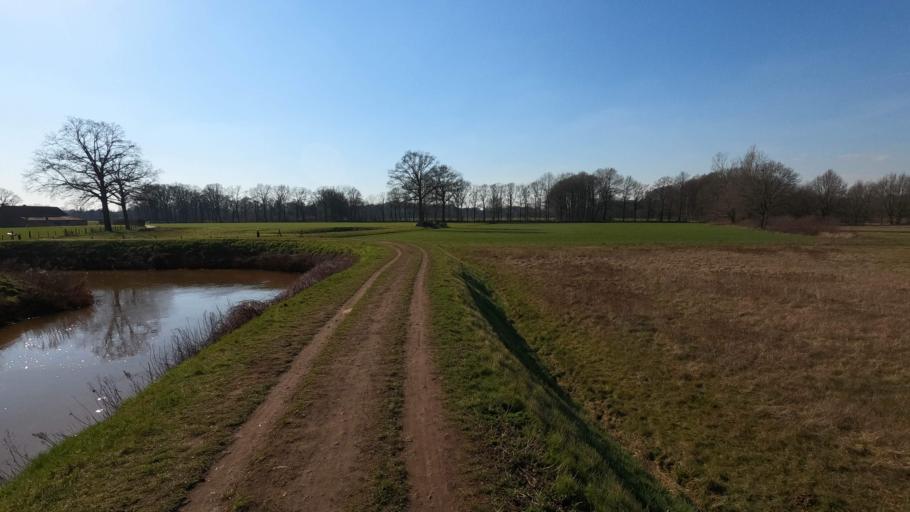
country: BE
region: Flanders
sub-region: Provincie Antwerpen
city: Herenthout
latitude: 51.1227
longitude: 4.7200
